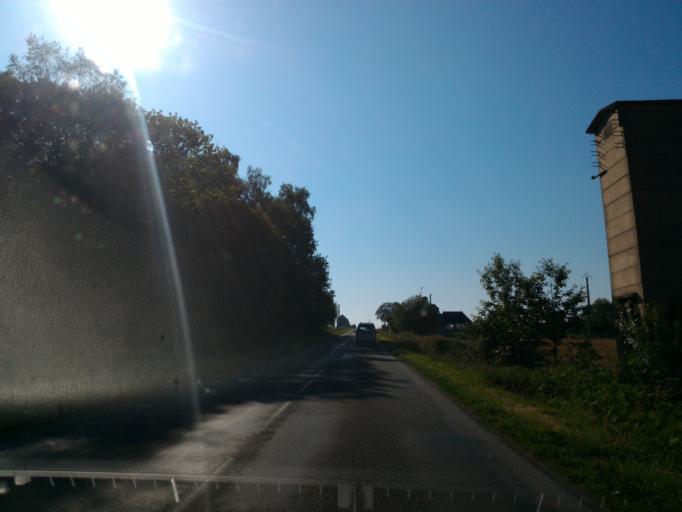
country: FR
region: Pays de la Loire
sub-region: Departement de la Mayenne
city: Juvigne
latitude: 48.2115
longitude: -1.0751
